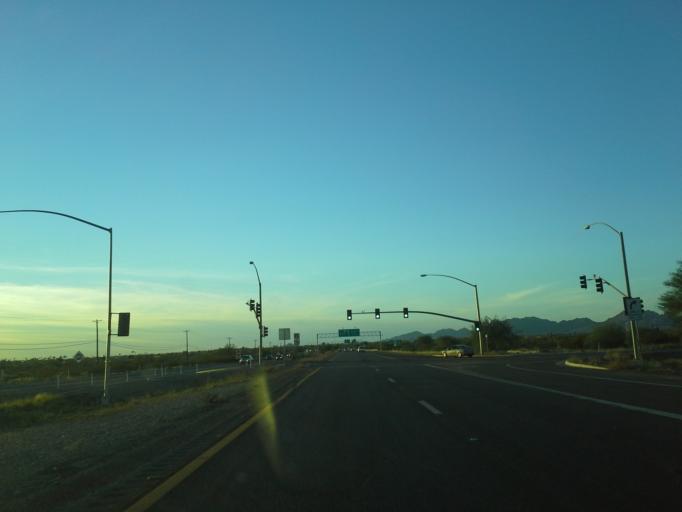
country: US
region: Arizona
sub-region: Pinal County
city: Apache Junction
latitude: 33.3827
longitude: -111.4943
